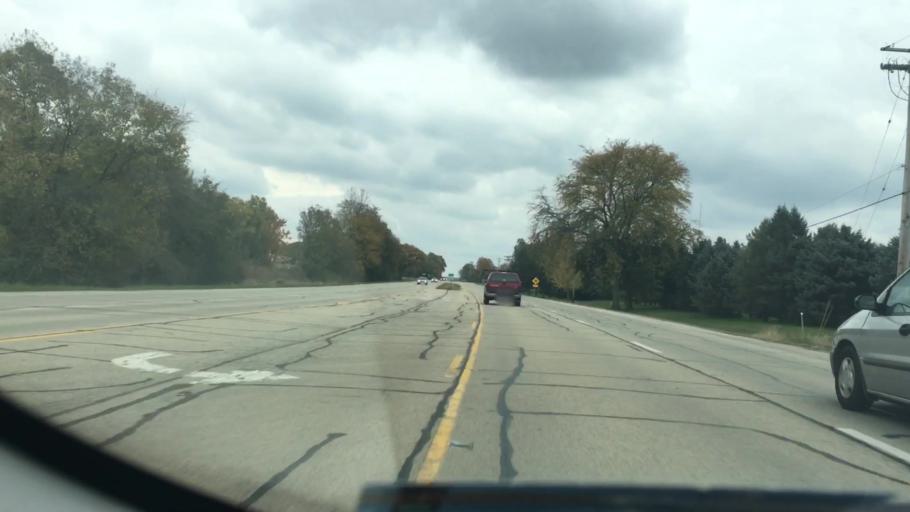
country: US
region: Illinois
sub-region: Peoria County
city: Peoria Heights
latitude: 40.7753
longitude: -89.5757
